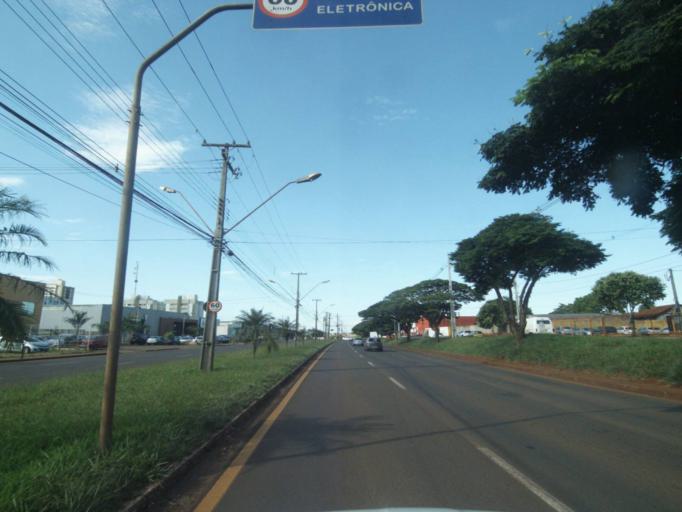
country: BR
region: Parana
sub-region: Londrina
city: Londrina
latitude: -23.3550
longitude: -51.1493
